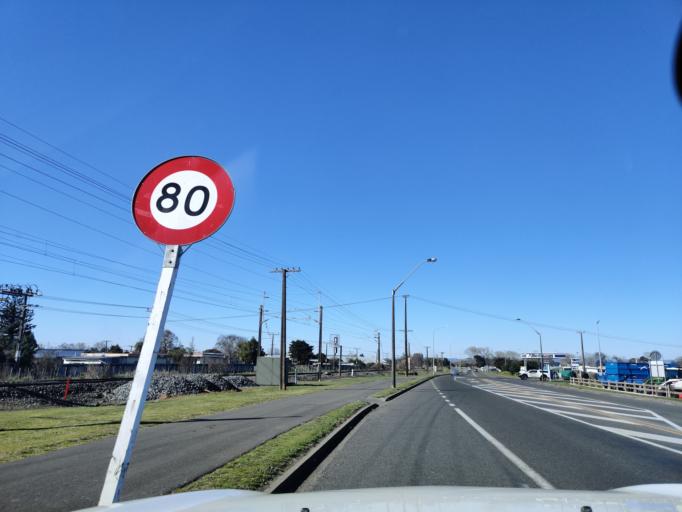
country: NZ
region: Manawatu-Wanganui
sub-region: Palmerston North City
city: Palmerston North
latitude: -40.2329
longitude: 175.5738
